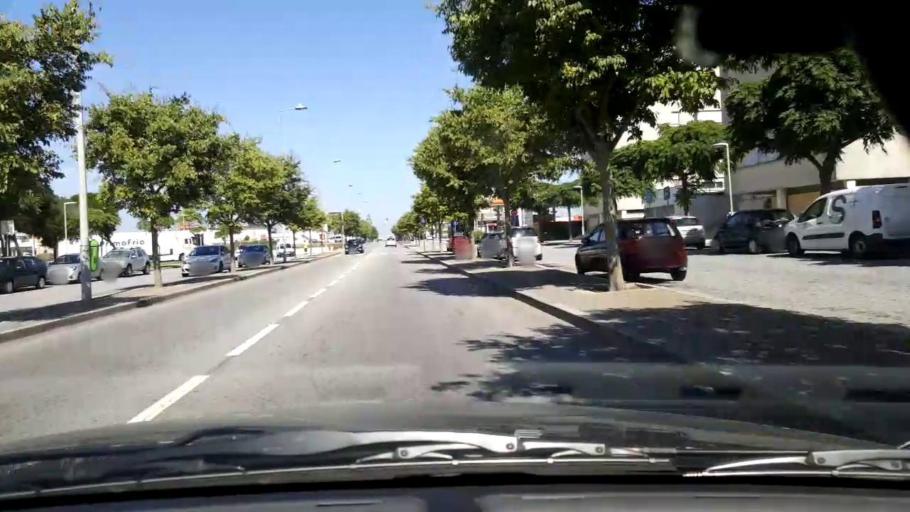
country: PT
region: Porto
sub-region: Vila do Conde
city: Vila do Conde
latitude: 41.3623
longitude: -8.7462
